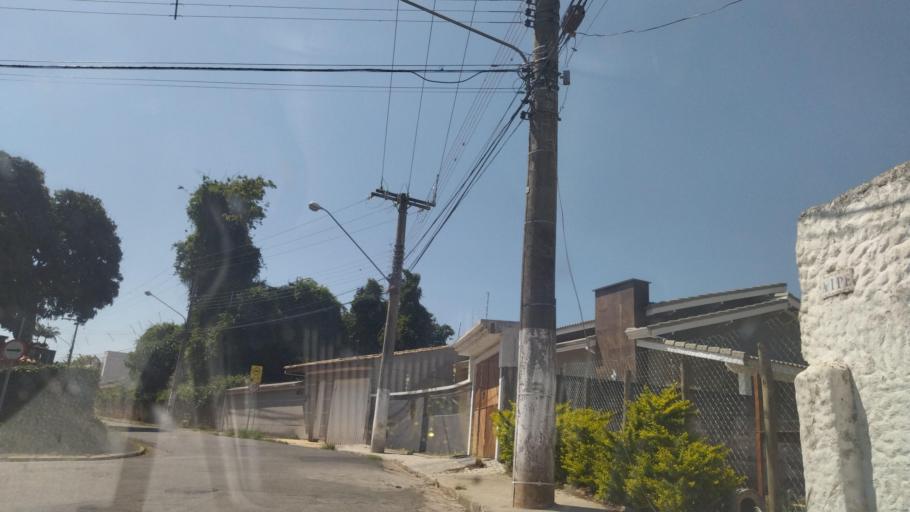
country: BR
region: Sao Paulo
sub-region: Atibaia
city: Atibaia
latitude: -23.1223
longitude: -46.5507
